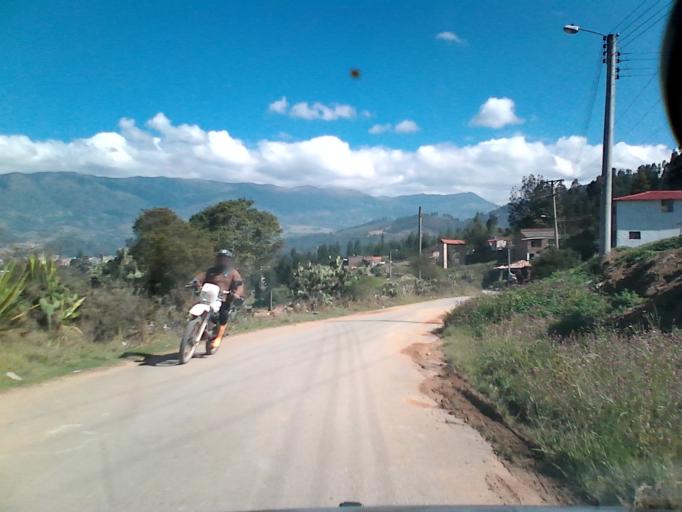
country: CO
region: Boyaca
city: Duitama
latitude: 5.7949
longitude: -73.0144
